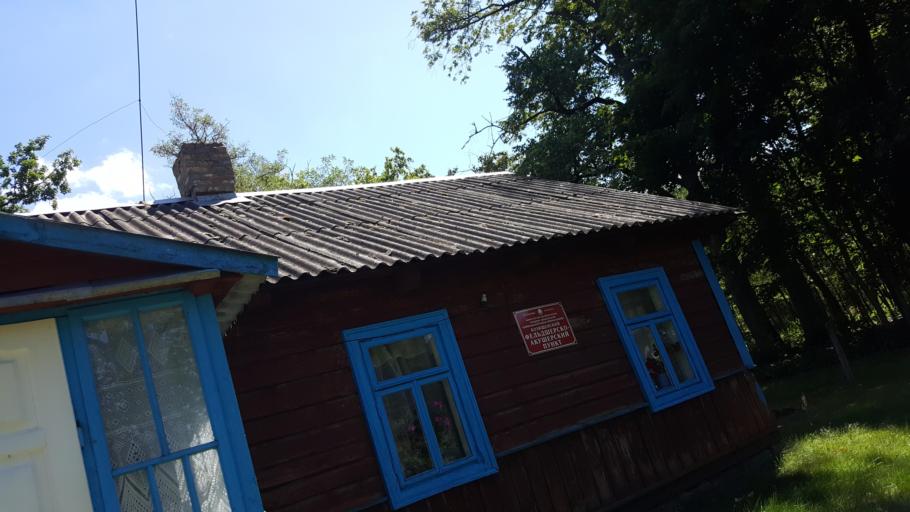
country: BY
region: Brest
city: Horad Kobryn
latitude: 52.3472
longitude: 24.3478
